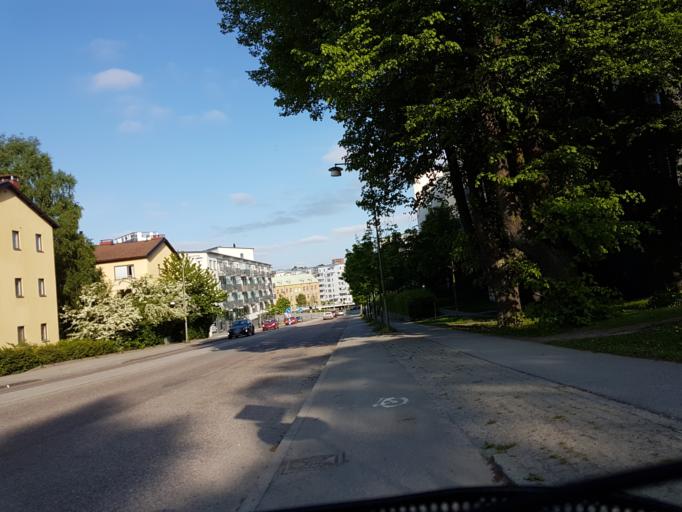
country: SE
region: Stockholm
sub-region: Sundbybergs Kommun
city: Sundbyberg
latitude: 59.3604
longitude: 17.9572
